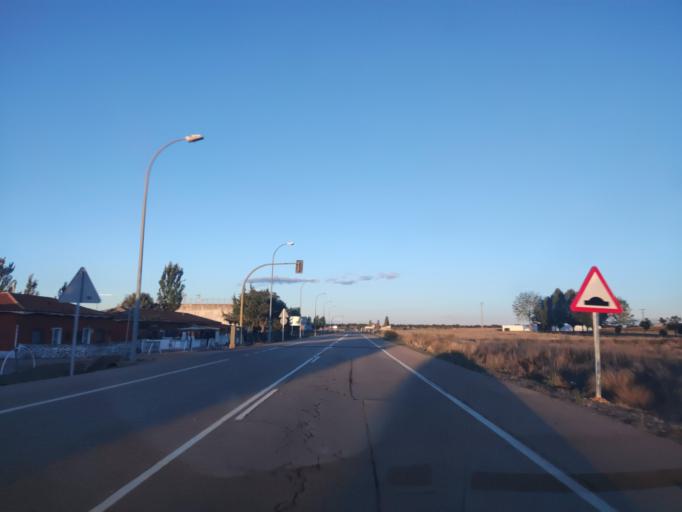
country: ES
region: Castille and Leon
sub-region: Provincia de Salamanca
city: Martin de Yeltes
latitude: 40.7756
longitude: -6.2868
